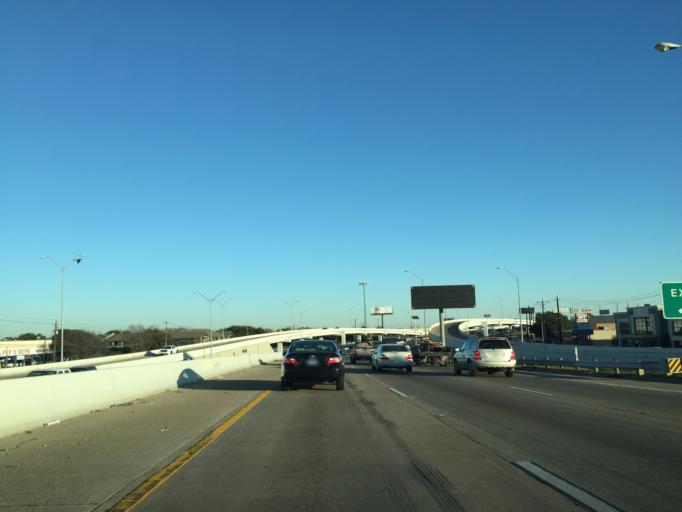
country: US
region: Texas
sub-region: Travis County
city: Wells Branch
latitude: 30.3712
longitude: -97.7223
